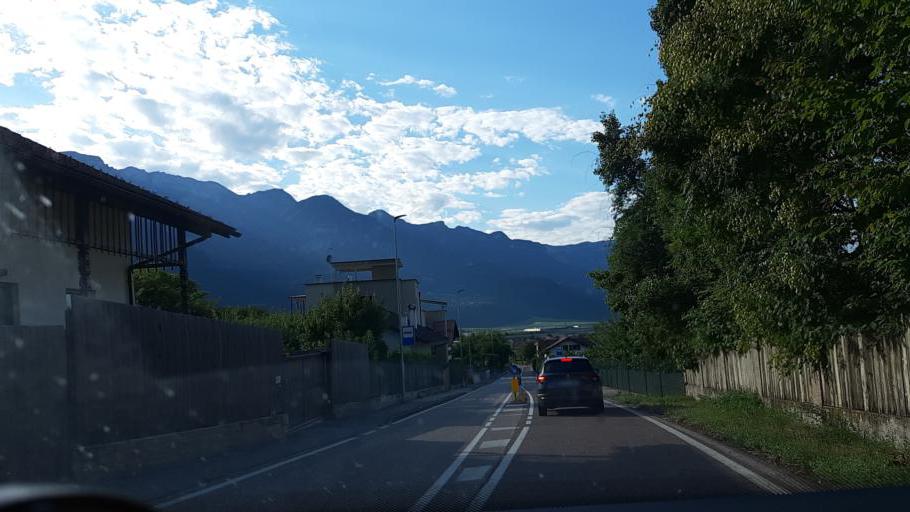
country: IT
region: Trentino-Alto Adige
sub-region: Bolzano
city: Egna
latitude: 46.3193
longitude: 11.2804
